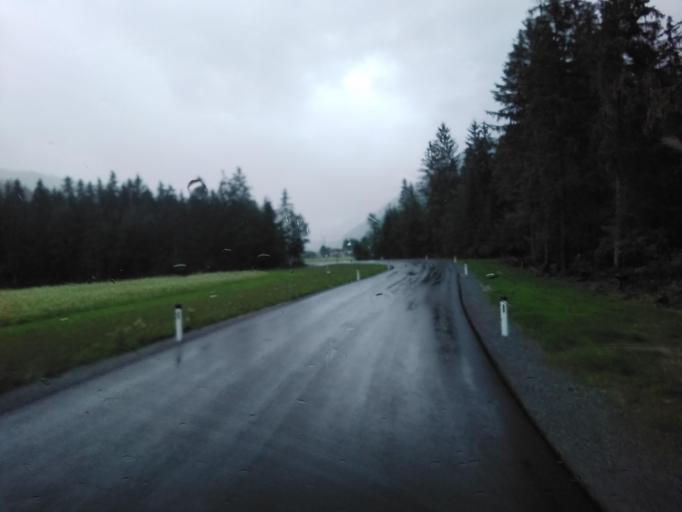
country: AT
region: Tyrol
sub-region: Politischer Bezirk Kitzbuhel
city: Schwendt
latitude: 47.5972
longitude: 12.3821
